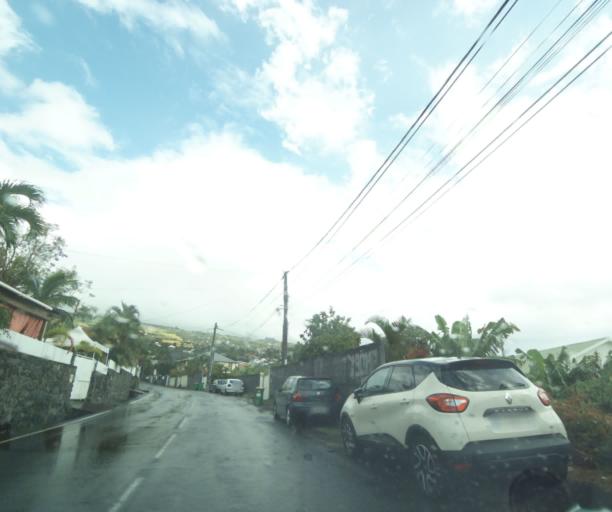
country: RE
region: Reunion
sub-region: Reunion
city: La Possession
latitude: -20.9822
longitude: 55.3285
